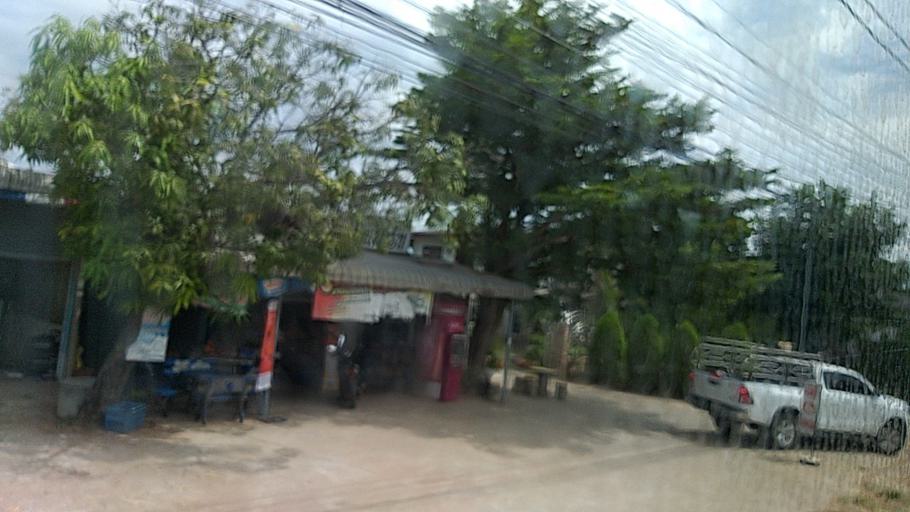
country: TH
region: Maha Sarakham
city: Chiang Yuen
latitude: 16.3475
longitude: 103.1224
